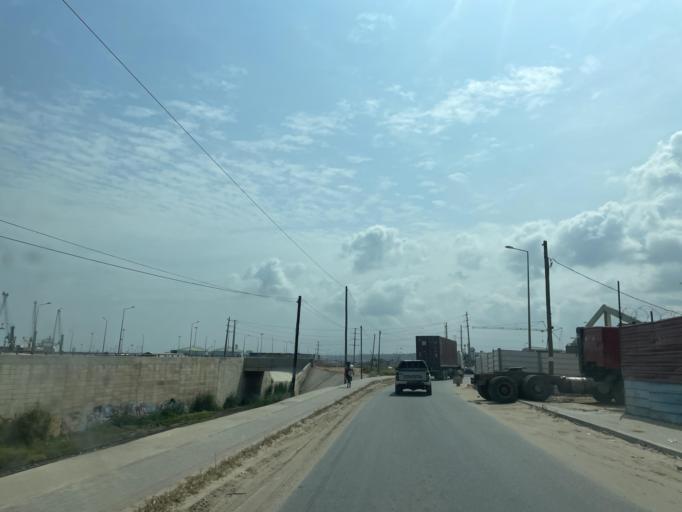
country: AO
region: Luanda
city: Luanda
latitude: -8.8036
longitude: 13.2488
